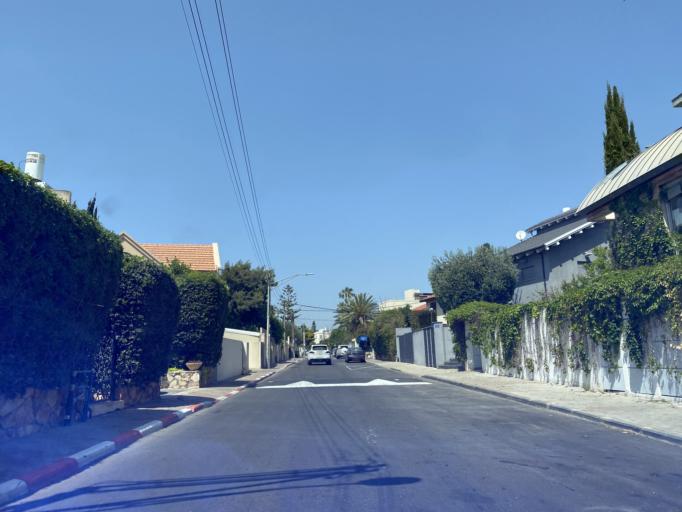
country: IL
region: Tel Aviv
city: Herzliya Pituah
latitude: 32.1712
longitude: 34.8100
